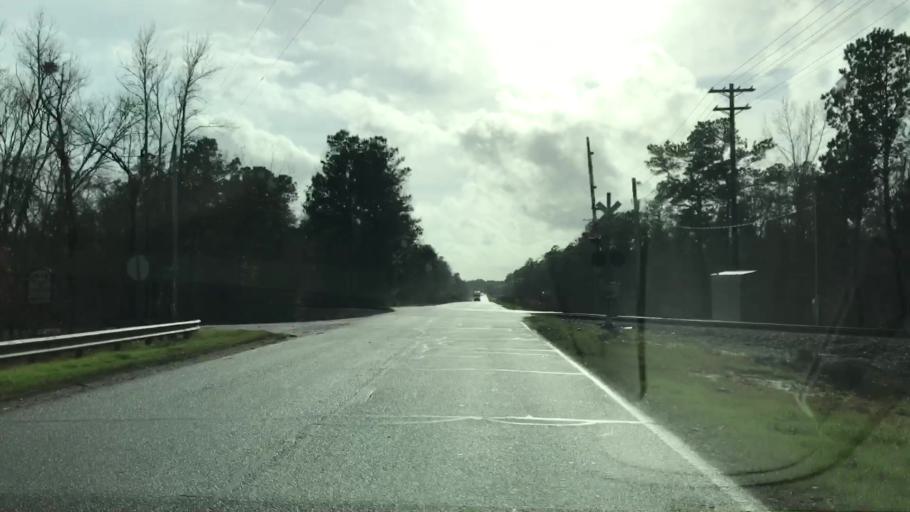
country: US
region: South Carolina
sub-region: Williamsburg County
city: Andrews
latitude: 33.4837
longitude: -79.5525
